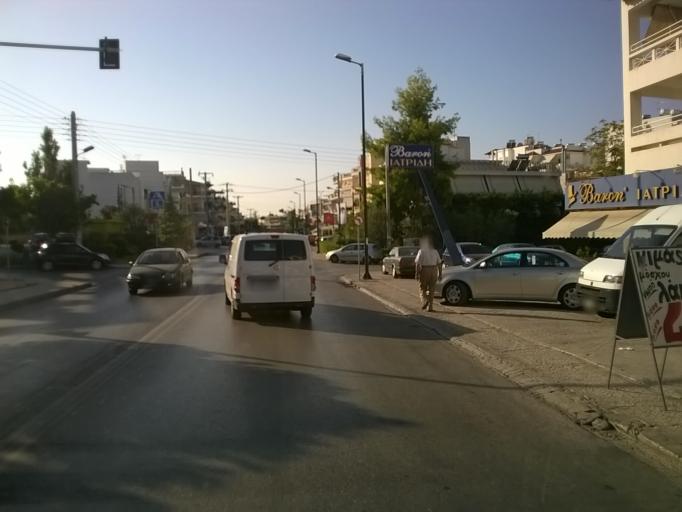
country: GR
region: Attica
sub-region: Nomarchia Athinas
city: Glyfada
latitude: 37.8747
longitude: 23.7640
